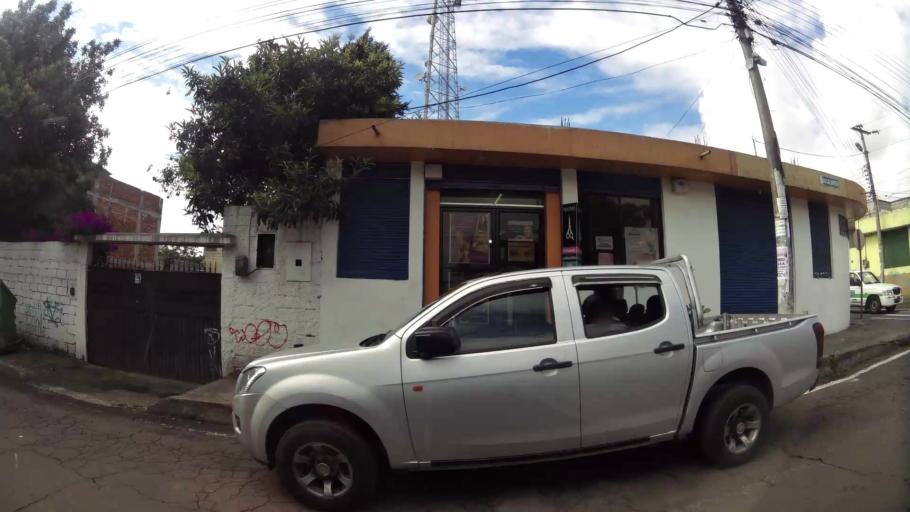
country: EC
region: Pichincha
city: Sangolqui
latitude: -0.3320
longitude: -78.4467
